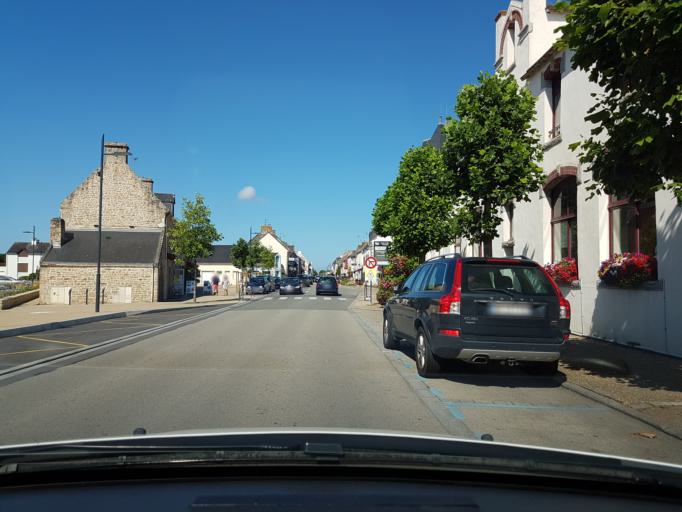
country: FR
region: Brittany
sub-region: Departement du Morbihan
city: Belz
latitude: 47.6758
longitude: -3.1684
